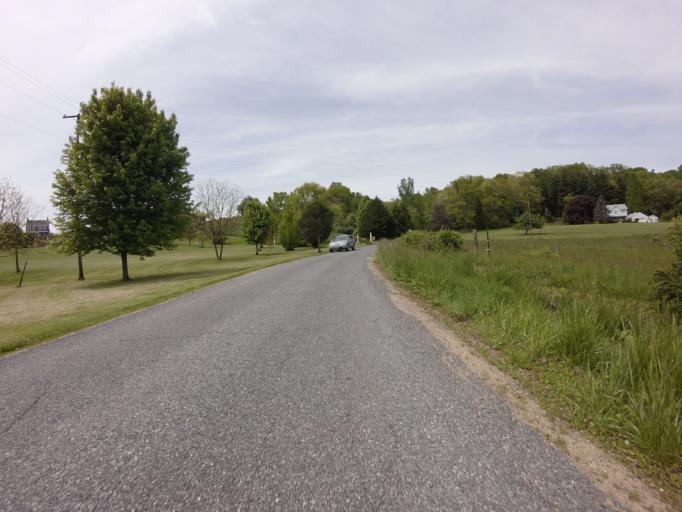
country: US
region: Maryland
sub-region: Carroll County
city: Eldersburg
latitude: 39.4787
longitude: -77.0020
